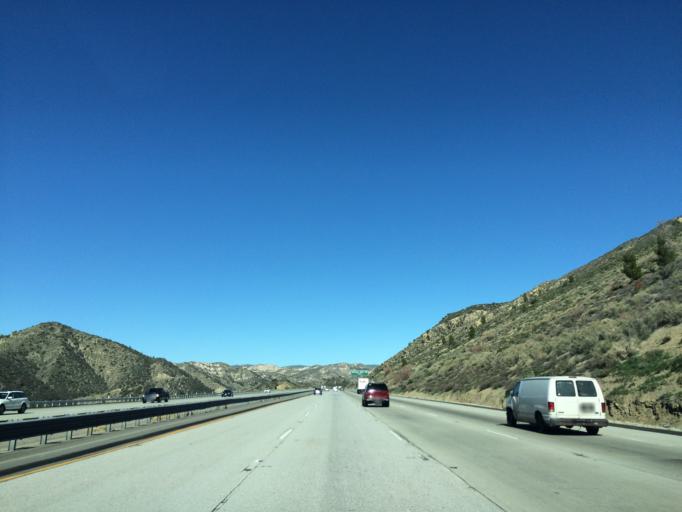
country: US
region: California
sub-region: Kern County
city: Lebec
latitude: 34.6898
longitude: -118.7876
